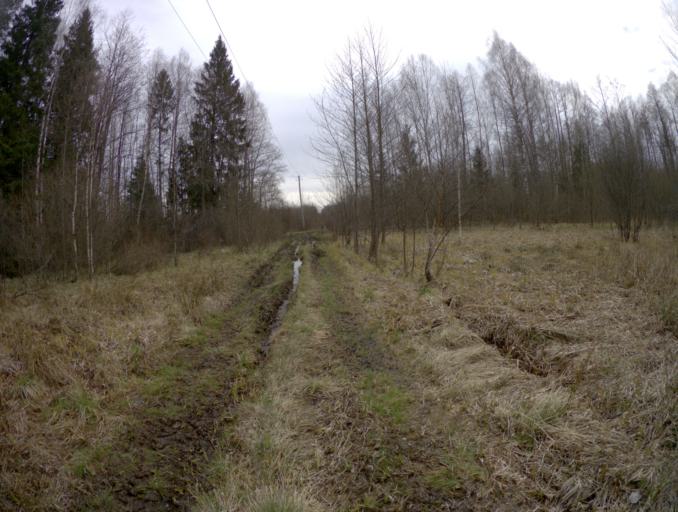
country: RU
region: Vladimir
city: Raduzhnyy
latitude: 55.8799
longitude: 40.2072
